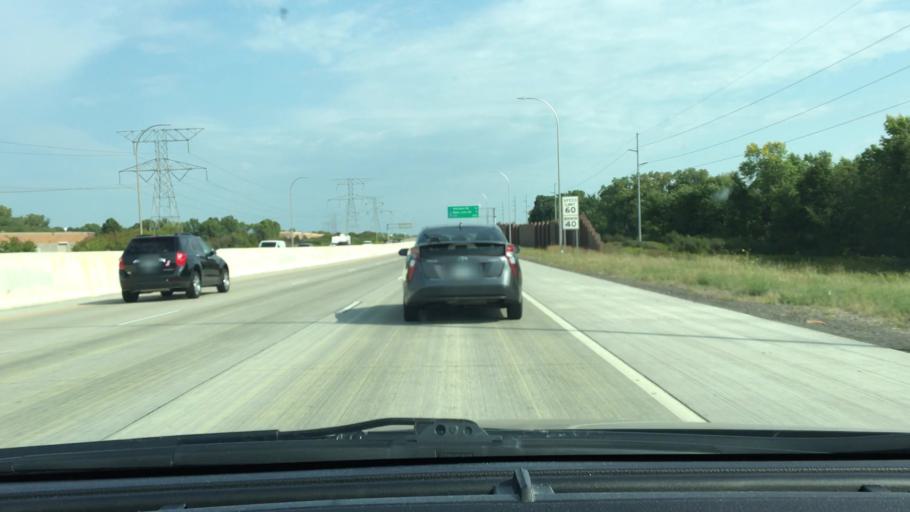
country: US
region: Minnesota
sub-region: Hennepin County
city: Plymouth
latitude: 45.0183
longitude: -93.4556
